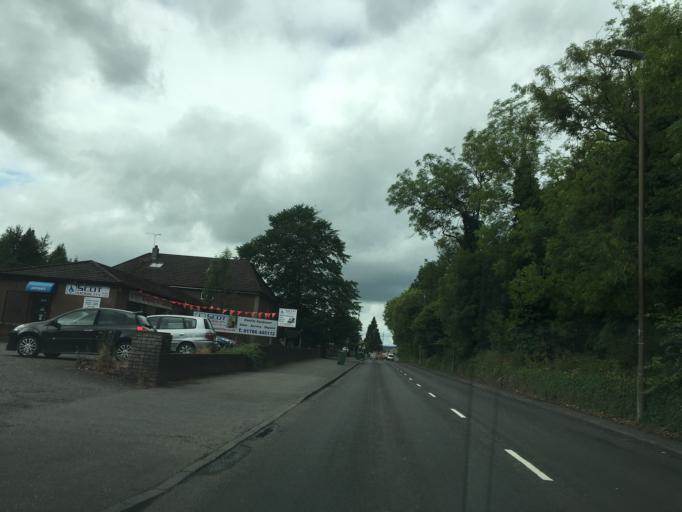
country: GB
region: Scotland
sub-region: Stirling
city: Stirling
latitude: 56.1353
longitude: -3.9164
